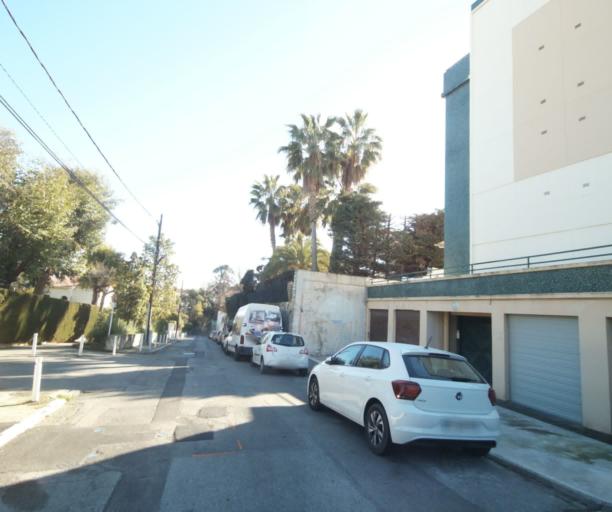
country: FR
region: Provence-Alpes-Cote d'Azur
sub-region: Departement des Alpes-Maritimes
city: Antibes
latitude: 43.5820
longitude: 7.1145
